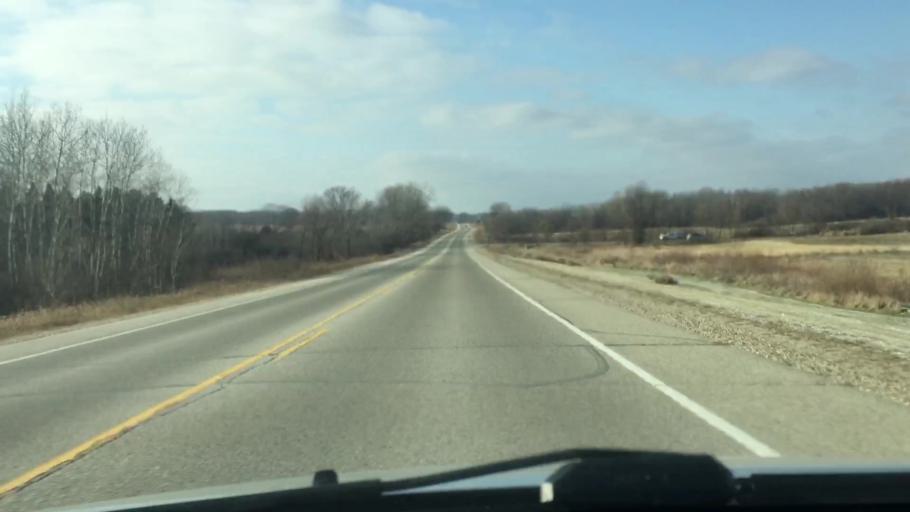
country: US
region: Wisconsin
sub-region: Waukesha County
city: Eagle
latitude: 42.8791
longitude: -88.5102
